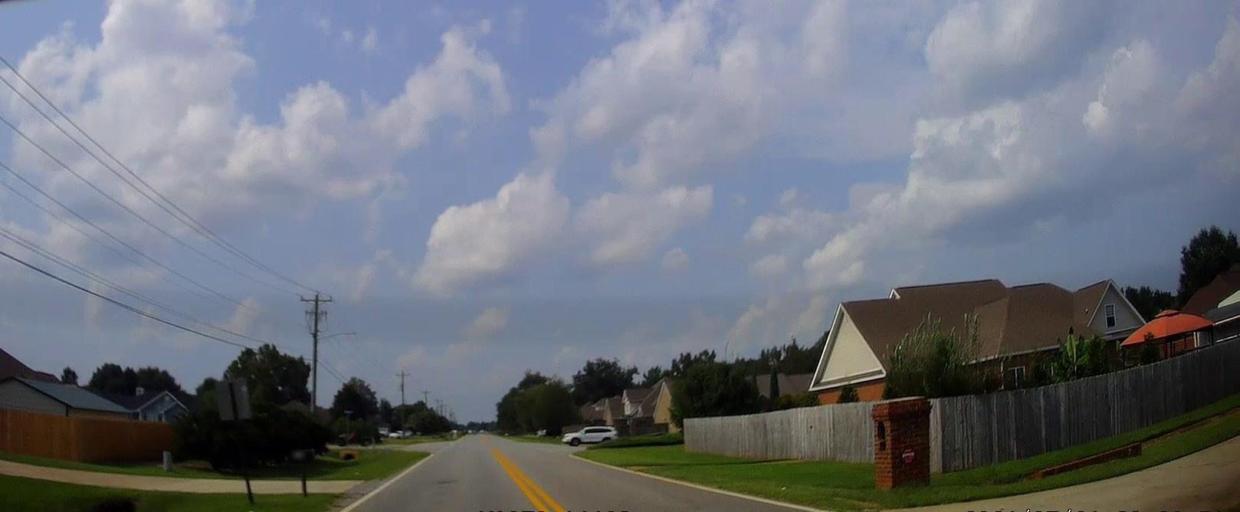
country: US
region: Georgia
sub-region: Houston County
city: Centerville
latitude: 32.5589
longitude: -83.6522
